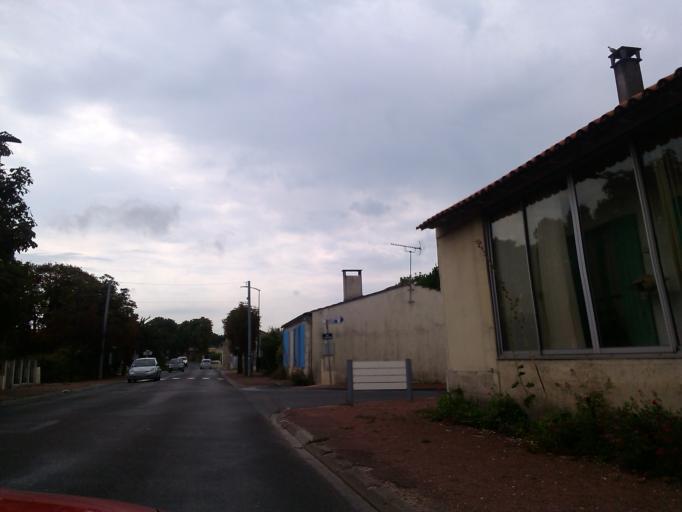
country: FR
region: Poitou-Charentes
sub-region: Departement de la Charente-Maritime
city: La Tremblade
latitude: 45.7620
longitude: -1.1419
